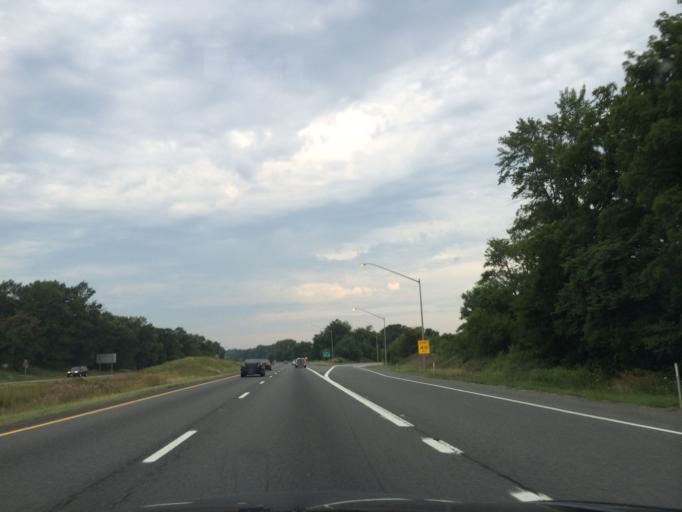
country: US
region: Maryland
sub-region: Washington County
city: Halfway
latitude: 39.6062
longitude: -77.7467
